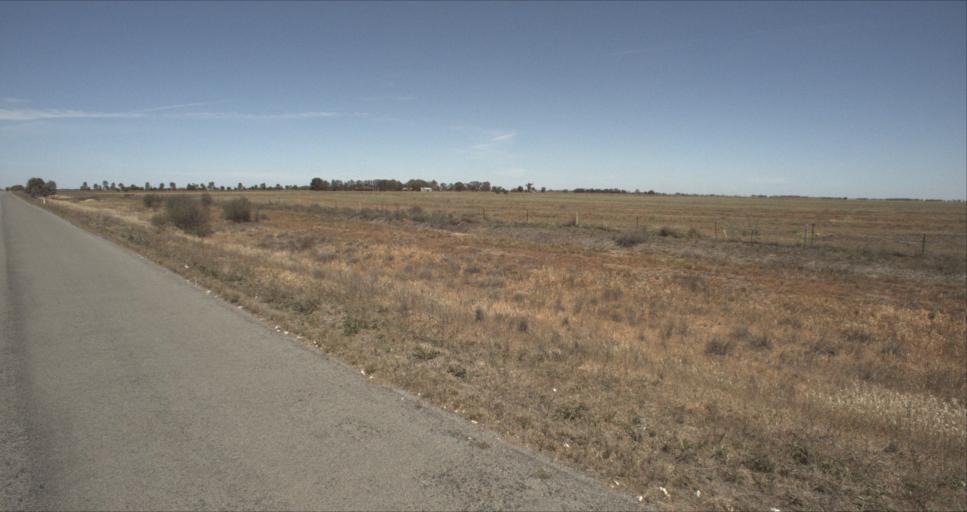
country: AU
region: New South Wales
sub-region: Leeton
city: Leeton
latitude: -34.4339
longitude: 146.2991
